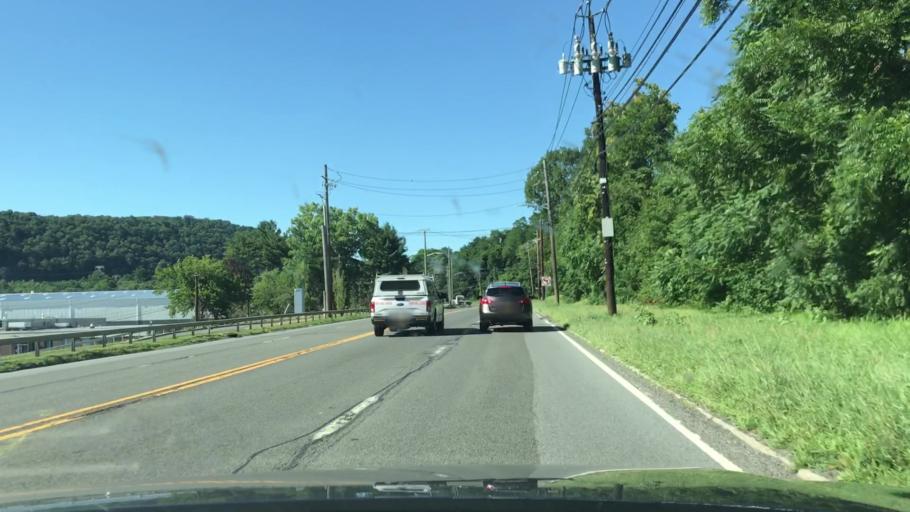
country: US
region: New York
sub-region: Westchester County
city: Hawthorne
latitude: 41.0973
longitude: -73.8085
